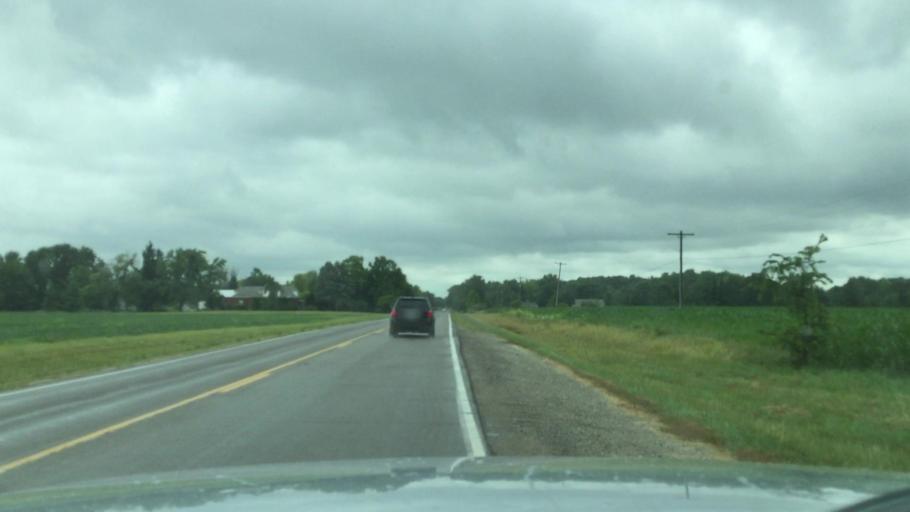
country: US
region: Michigan
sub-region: Genesee County
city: Clio
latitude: 43.1190
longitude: -83.7738
